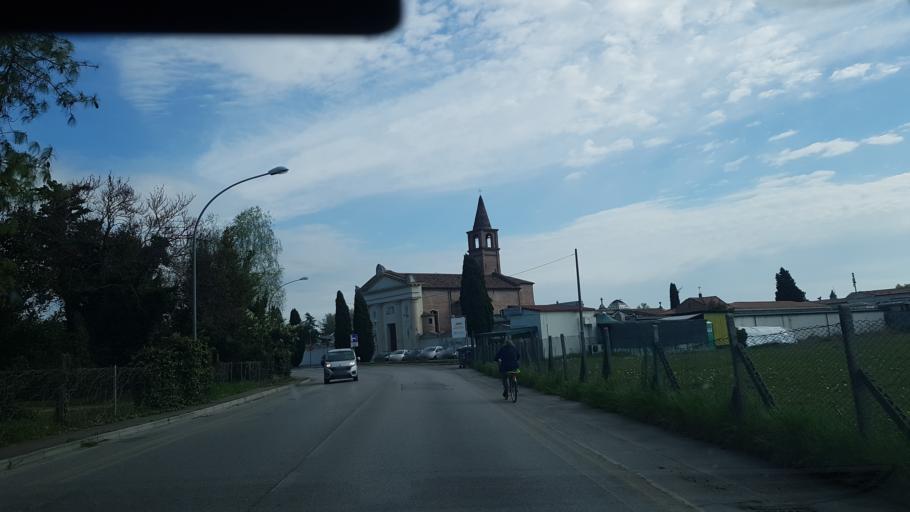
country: IT
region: Veneto
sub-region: Provincia di Rovigo
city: Rovigo
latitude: 45.0688
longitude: 11.8007
